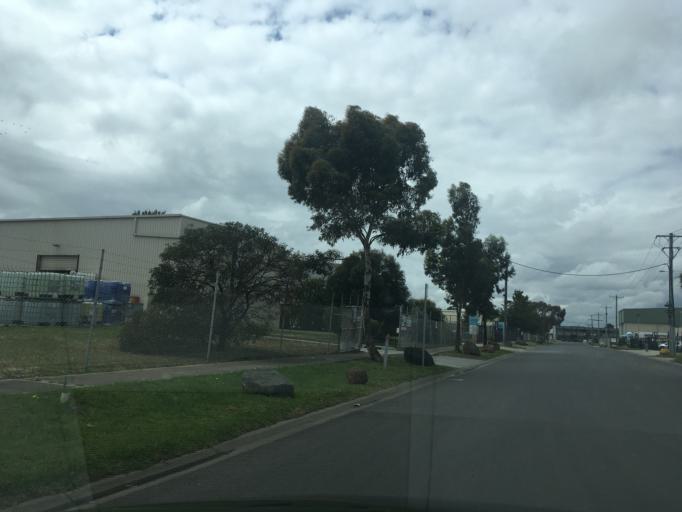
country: AU
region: Victoria
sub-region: Brimbank
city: Sunshine West
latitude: -37.8211
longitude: 144.8043
